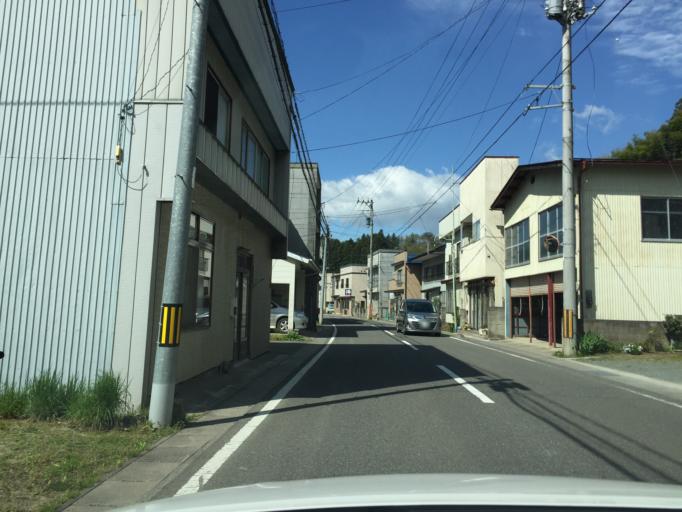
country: JP
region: Fukushima
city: Funehikimachi-funehiki
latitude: 37.5335
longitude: 140.6150
